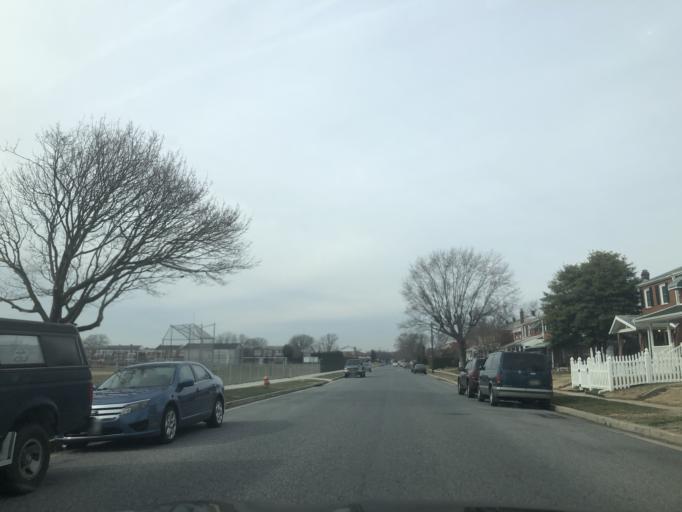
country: US
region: Maryland
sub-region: Baltimore County
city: Dundalk
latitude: 39.2675
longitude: -76.4860
